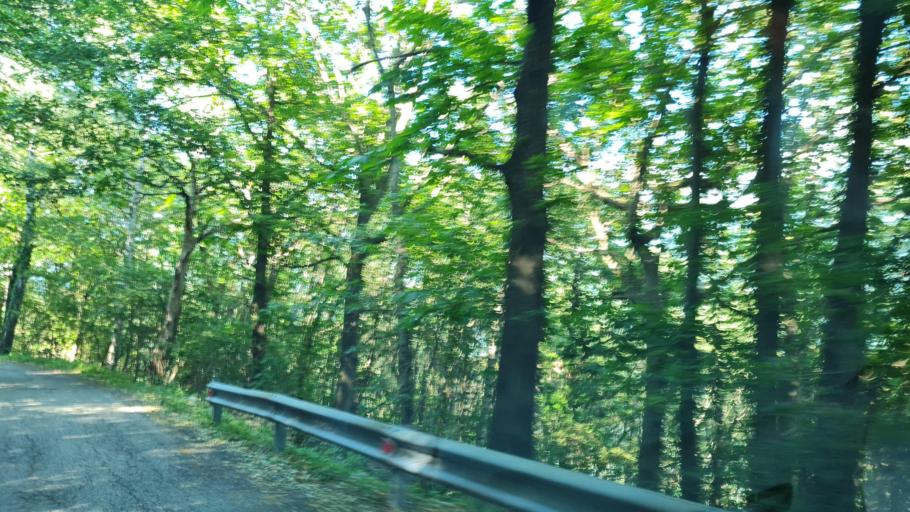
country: IT
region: Piedmont
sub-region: Provincia di Torino
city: Quincinetto
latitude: 45.5555
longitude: 7.7946
